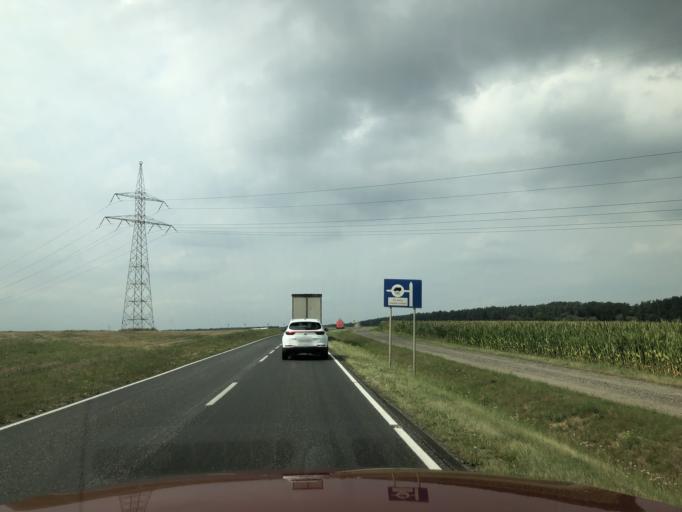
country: PL
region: Greater Poland Voivodeship
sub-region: Powiat leszczynski
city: Swieciechowa
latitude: 51.8613
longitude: 16.4901
